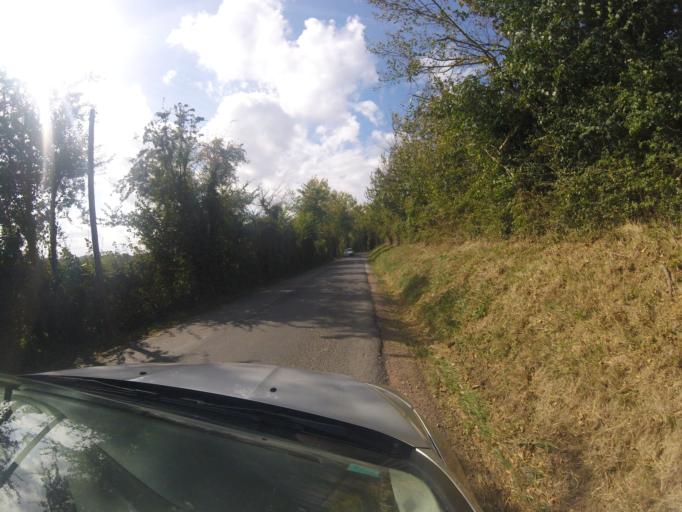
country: FR
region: Lower Normandy
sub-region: Departement du Calvados
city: Saint-Vigor-le-Grand
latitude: 49.3197
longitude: -0.6370
